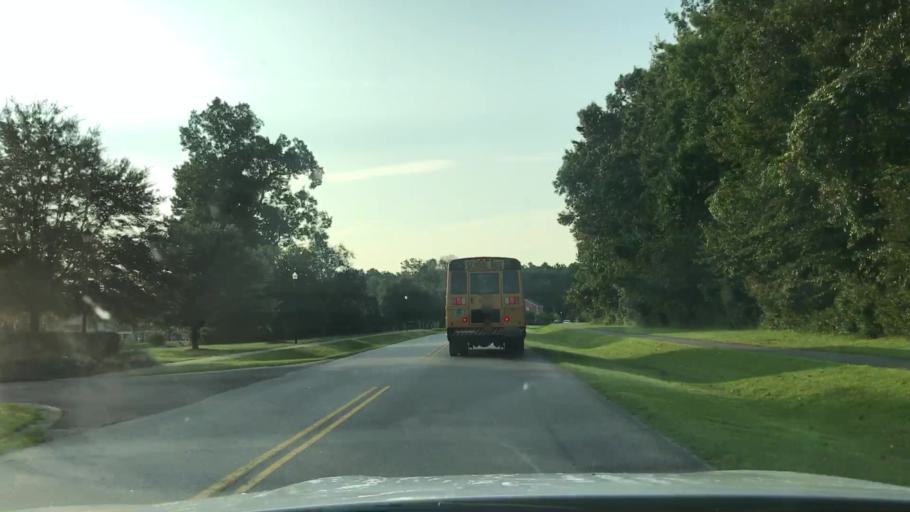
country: US
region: South Carolina
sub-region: Charleston County
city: Shell Point
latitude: 32.8331
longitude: -80.0902
